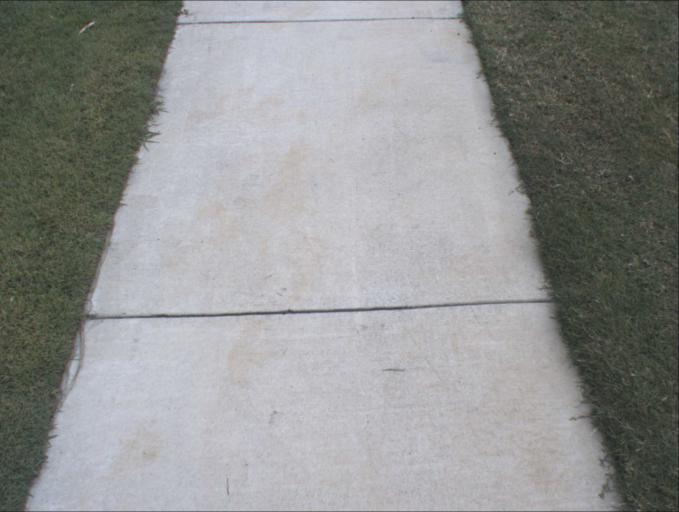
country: AU
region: Queensland
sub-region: Brisbane
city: Sunnybank Hills
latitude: -27.6682
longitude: 153.0410
